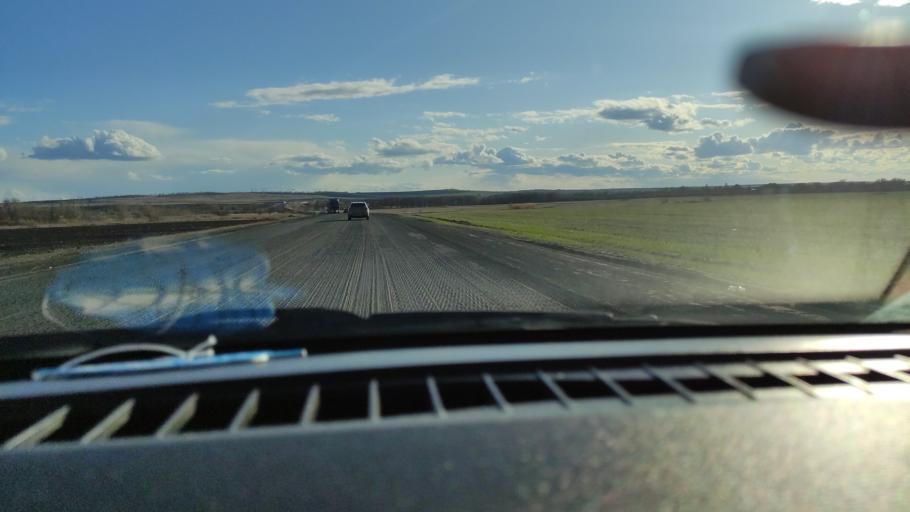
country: RU
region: Saratov
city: Yelshanka
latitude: 51.8068
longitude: 46.1951
